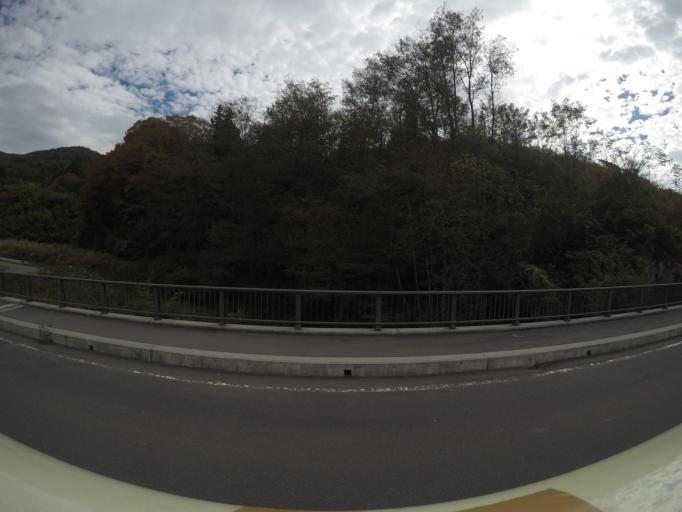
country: JP
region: Nagano
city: Chino
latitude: 35.8892
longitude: 138.0975
